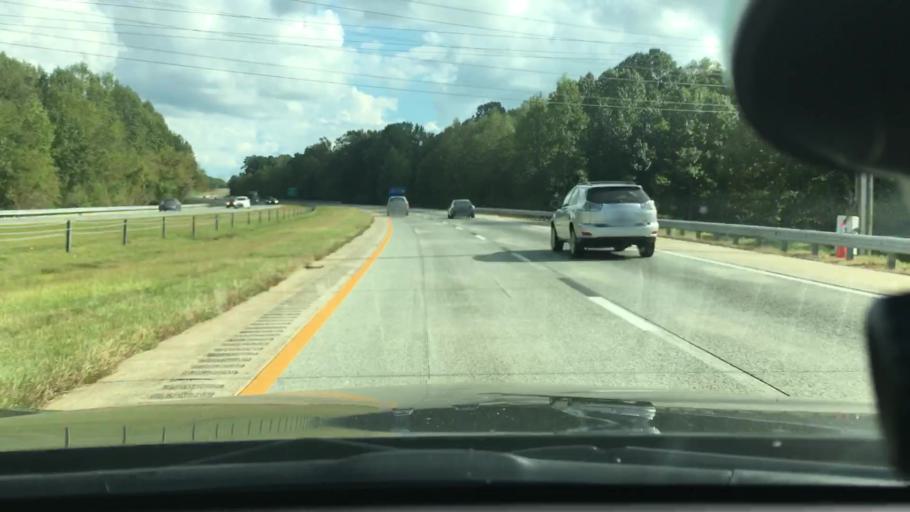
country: US
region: North Carolina
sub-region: Orange County
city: Chapel Hill
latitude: 35.9758
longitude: -79.0692
